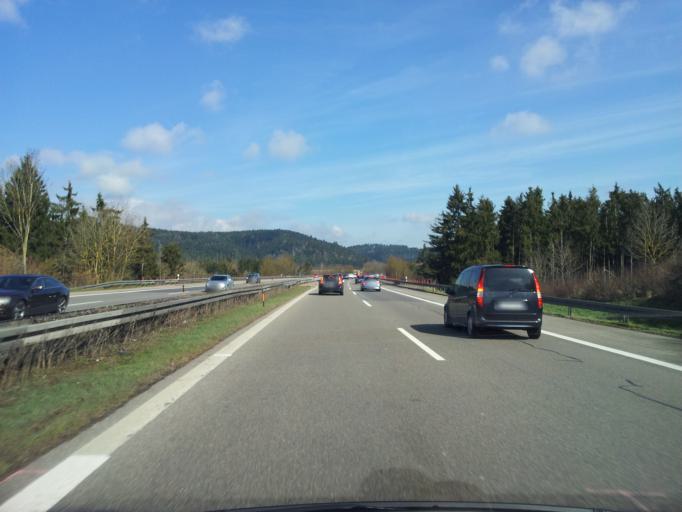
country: DE
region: Baden-Wuerttemberg
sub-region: Freiburg Region
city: Epfendorf
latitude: 48.2696
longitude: 8.6383
